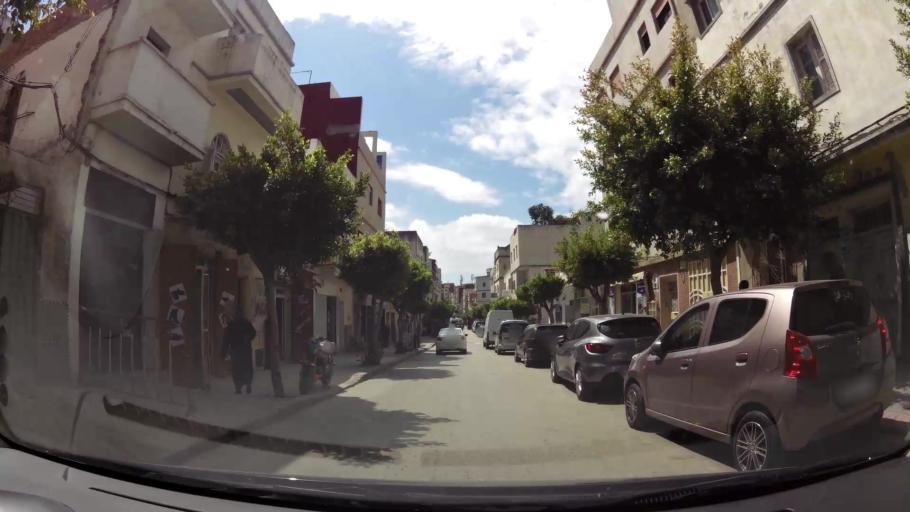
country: MA
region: Tanger-Tetouan
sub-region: Tanger-Assilah
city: Tangier
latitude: 35.7671
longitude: -5.8274
